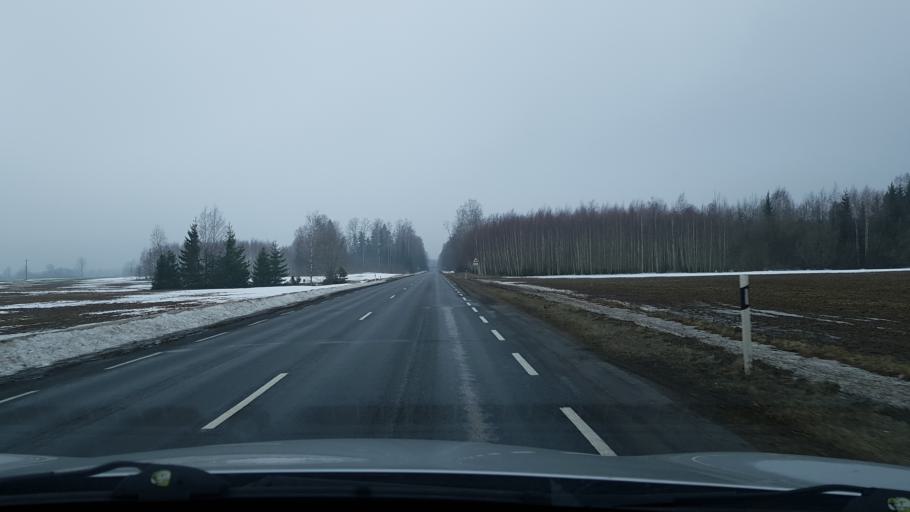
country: EE
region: Viljandimaa
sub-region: Viiratsi vald
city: Viiratsi
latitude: 58.2512
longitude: 25.8155
